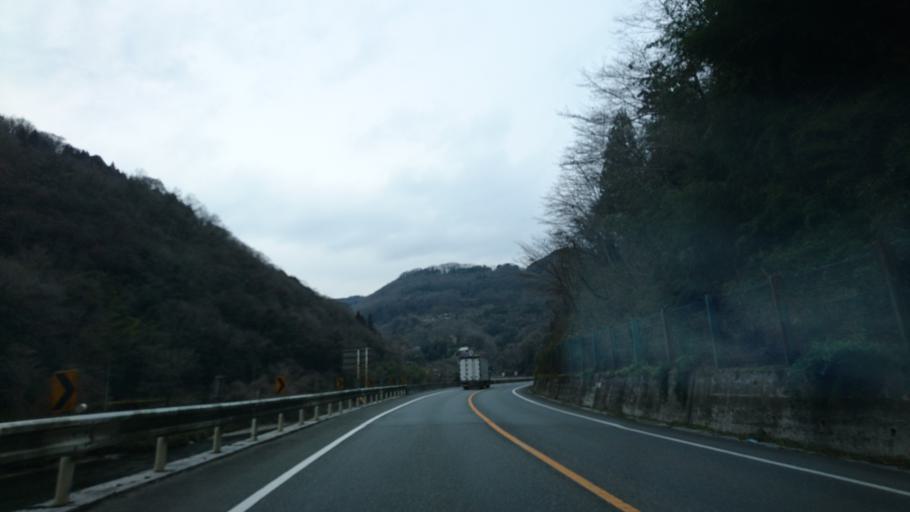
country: JP
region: Okayama
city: Niimi
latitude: 34.9147
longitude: 133.5213
